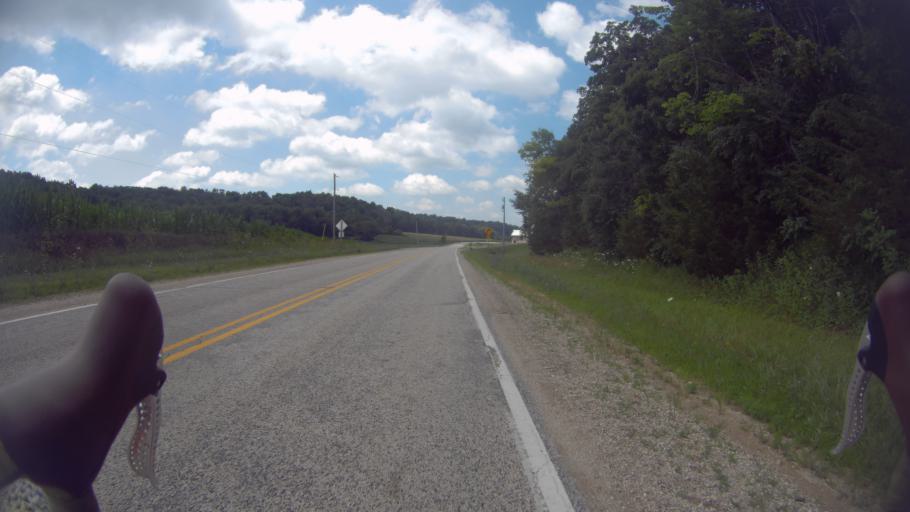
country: US
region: Wisconsin
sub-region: Sauk County
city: Sauk City
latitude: 43.2476
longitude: -89.6184
